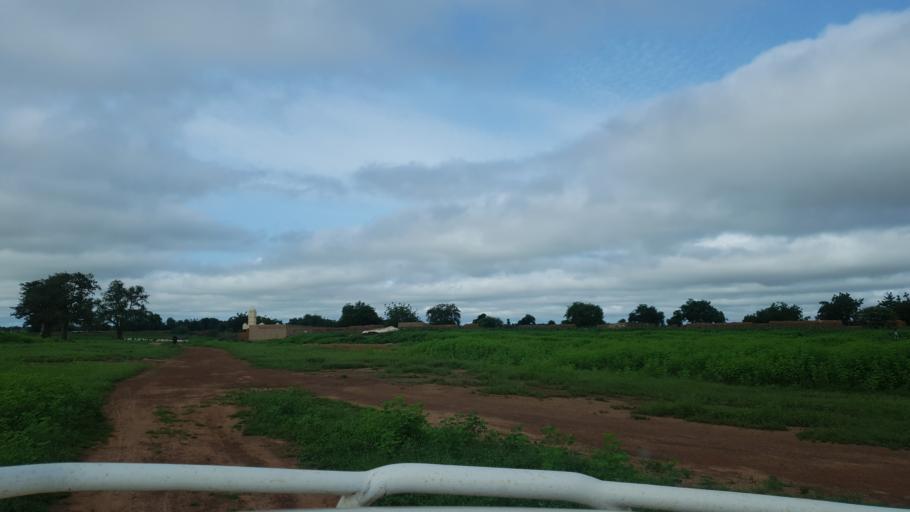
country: ML
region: Segou
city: Baroueli
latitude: 13.5089
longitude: -6.8984
